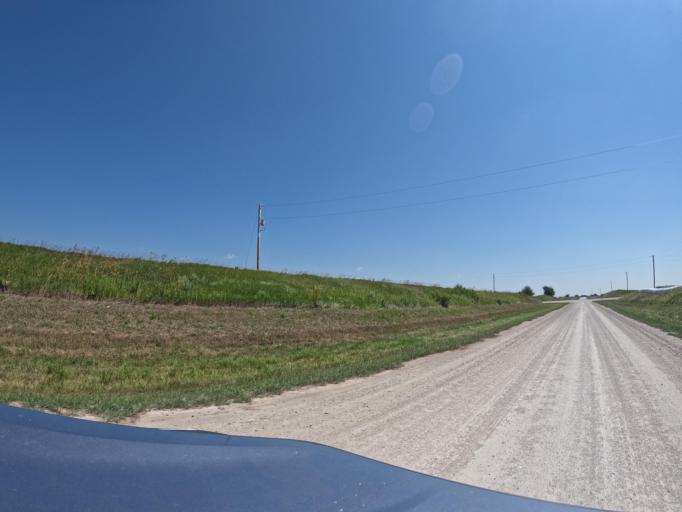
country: US
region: Iowa
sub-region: Keokuk County
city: Sigourney
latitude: 41.2505
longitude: -92.2063
